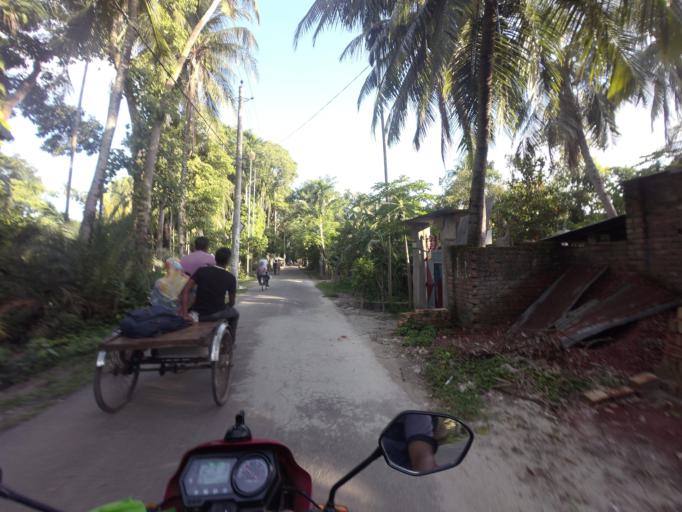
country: BD
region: Khulna
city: Khulna
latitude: 22.9037
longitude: 89.5214
